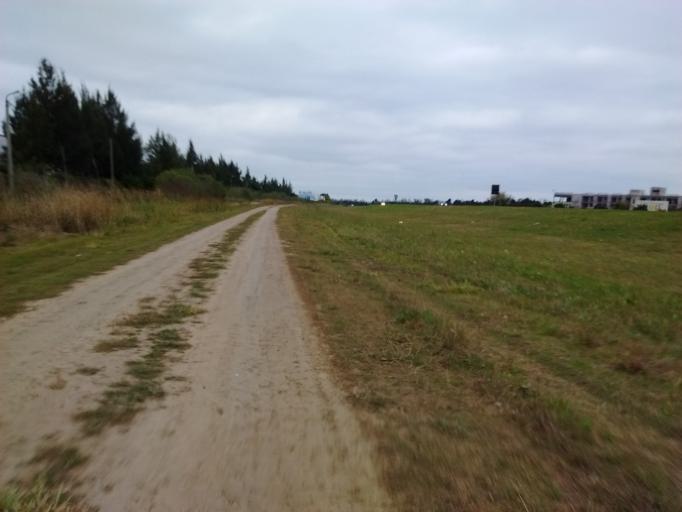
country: AR
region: Santa Fe
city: Funes
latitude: -32.9343
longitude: -60.8333
